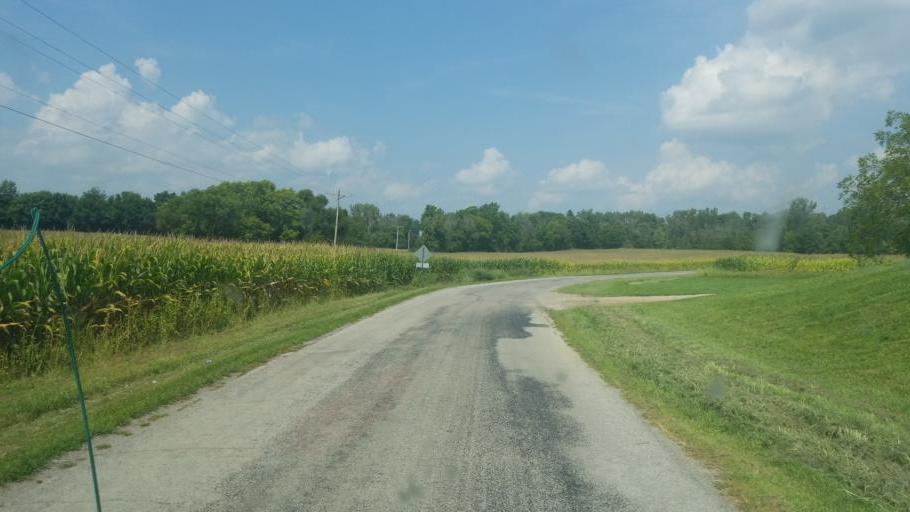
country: US
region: Ohio
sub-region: Richland County
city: Shelby
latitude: 40.8890
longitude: -82.5955
